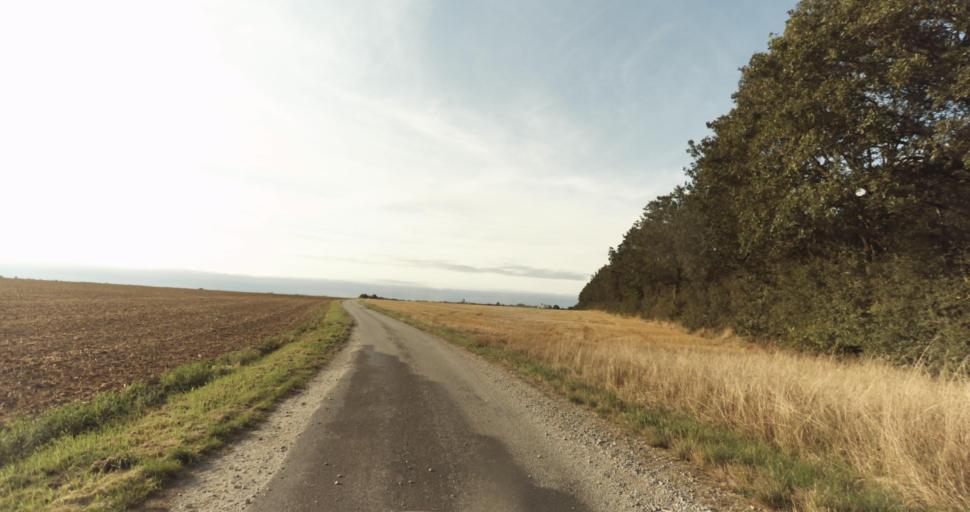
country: FR
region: Haute-Normandie
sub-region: Departement de l'Eure
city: Marcilly-sur-Eure
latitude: 48.8833
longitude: 1.2780
